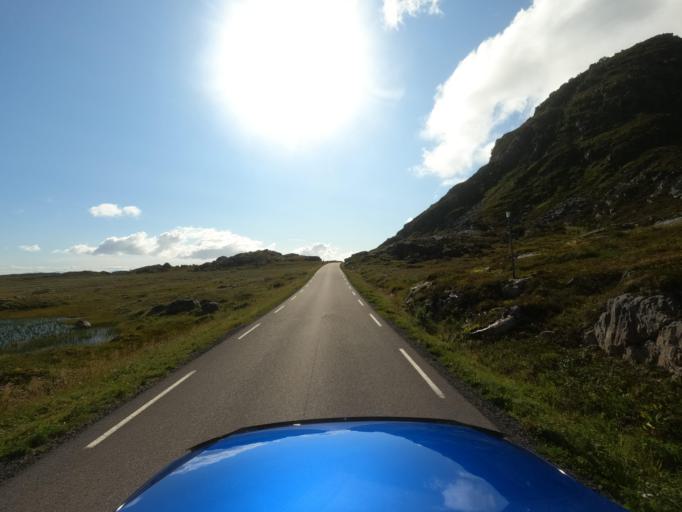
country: NO
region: Nordland
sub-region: Vestvagoy
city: Evjen
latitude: 68.1995
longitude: 14.0361
